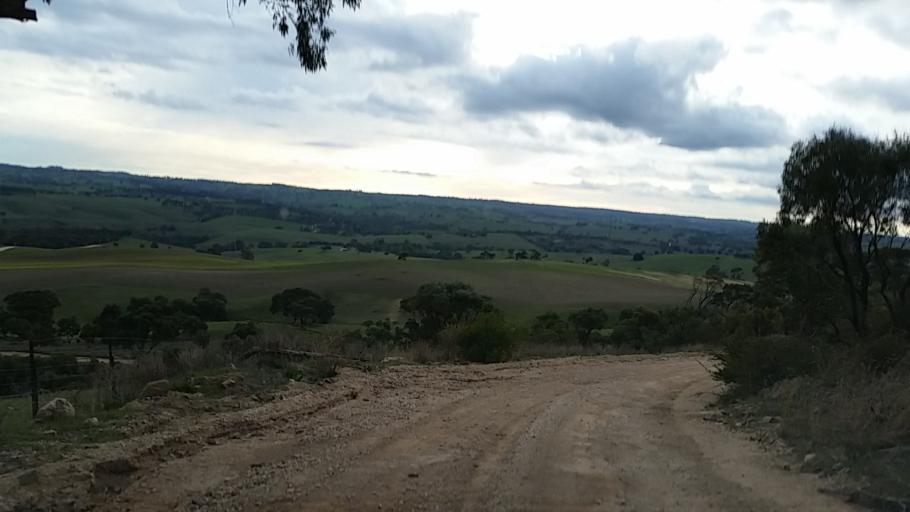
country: AU
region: South Australia
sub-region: Mount Barker
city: Callington
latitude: -34.9996
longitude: 139.0525
